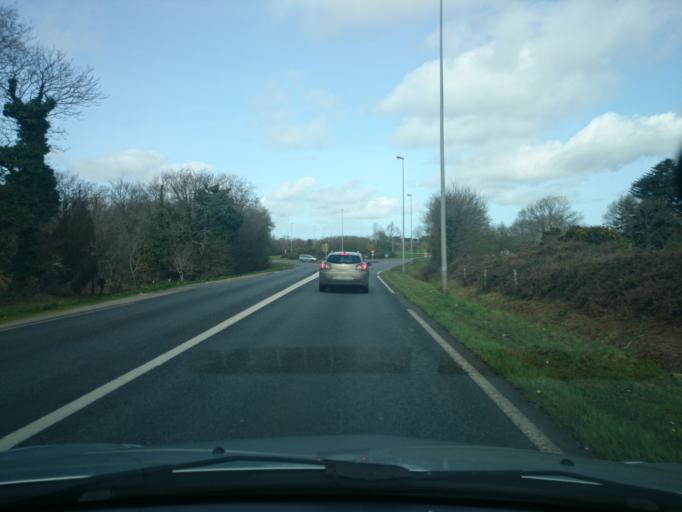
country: FR
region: Brittany
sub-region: Departement du Finistere
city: Gouesnou
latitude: 48.4429
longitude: -4.4550
